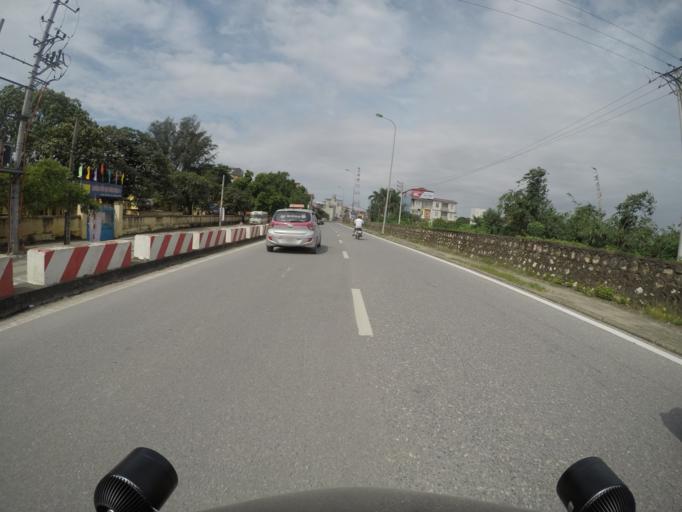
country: VN
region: Ha Noi
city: Tay Ho
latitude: 21.0919
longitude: 105.7838
